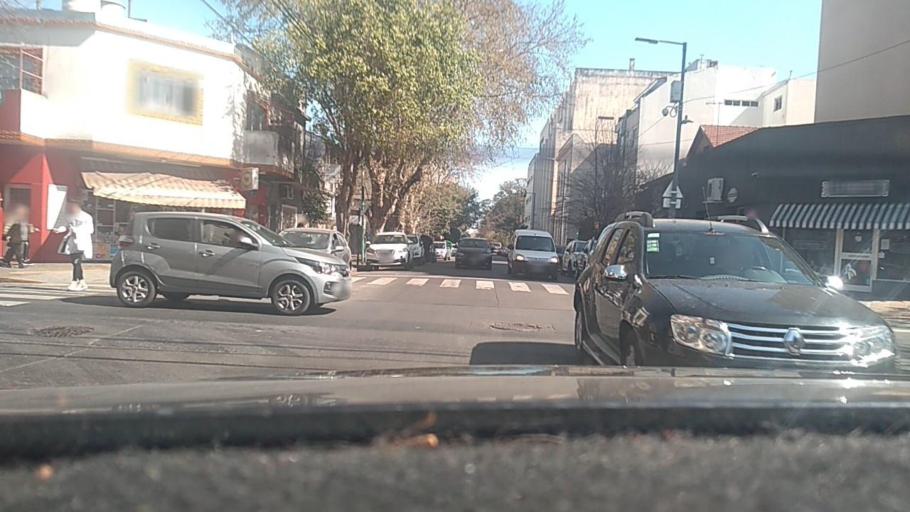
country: AR
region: Buenos Aires F.D.
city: Villa Santa Rita
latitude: -34.6048
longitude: -58.4904
